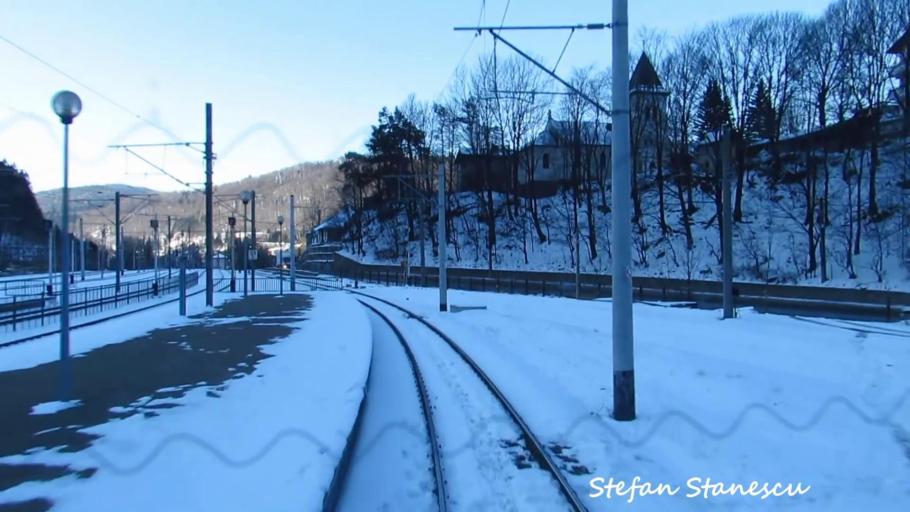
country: RO
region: Prahova
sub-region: Oras Sinaia
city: Sinaia
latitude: 45.3532
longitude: 25.5540
